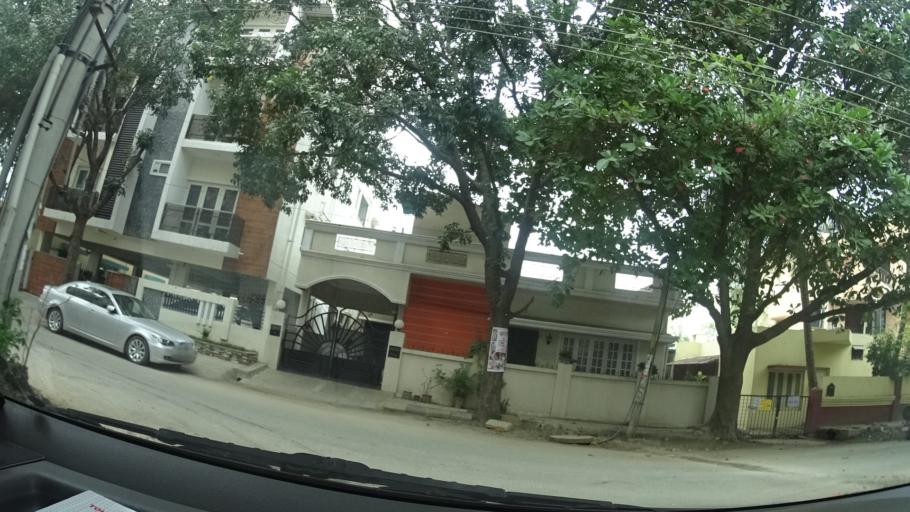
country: IN
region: Karnataka
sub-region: Bangalore Urban
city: Bangalore
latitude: 13.0272
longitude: 77.6263
